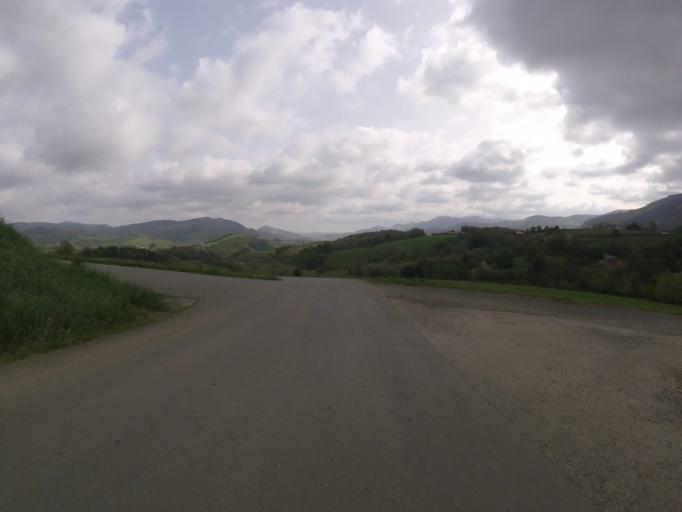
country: ES
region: Basque Country
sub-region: Provincia de Guipuzcoa
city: Irura
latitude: 43.1795
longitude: -2.0817
